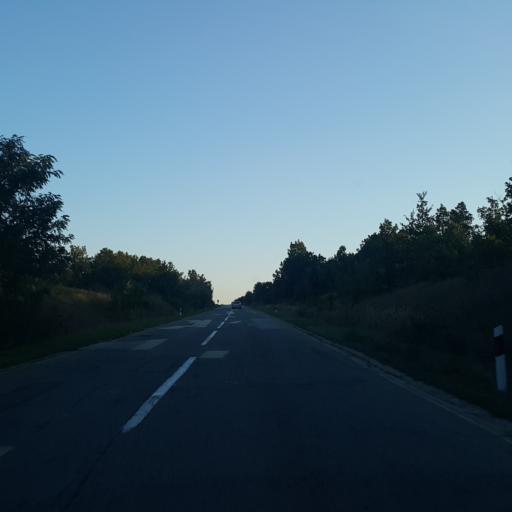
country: RS
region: Central Serbia
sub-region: Borski Okrug
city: Negotin
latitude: 44.1590
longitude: 22.3608
